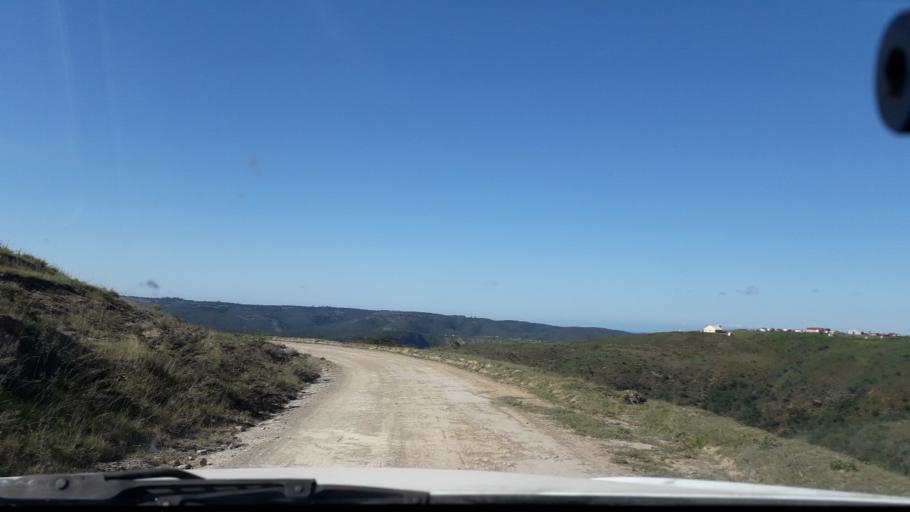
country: ZA
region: Eastern Cape
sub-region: Amathole District Municipality
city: Komga
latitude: -32.7861
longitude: 27.9543
